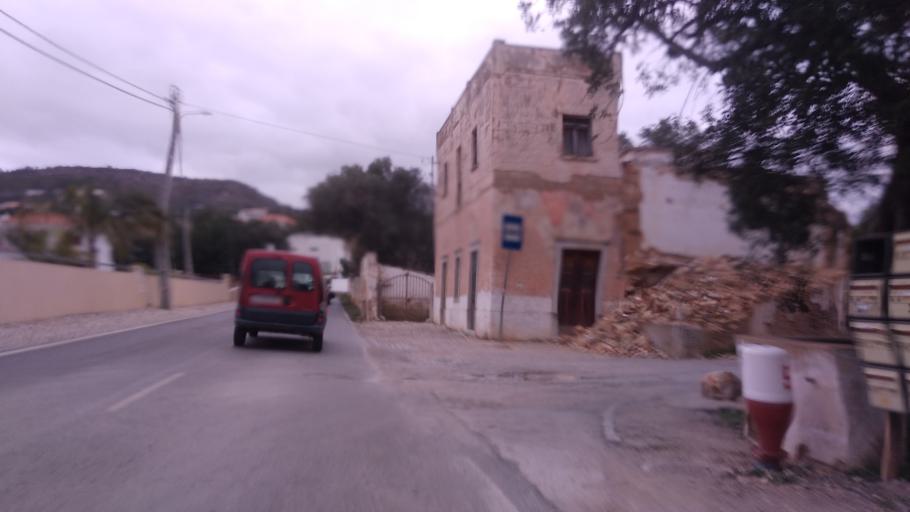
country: PT
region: Faro
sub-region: Faro
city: Santa Barbara de Nexe
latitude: 37.1079
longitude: -7.9618
